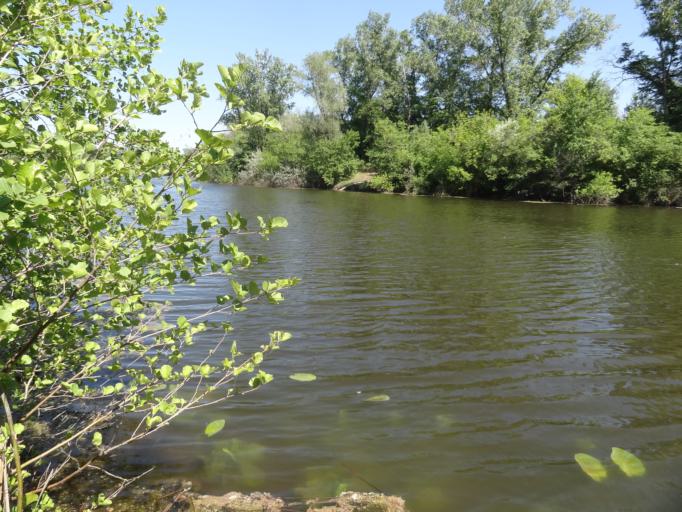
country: RU
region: Saratov
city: Engel's
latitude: 51.4665
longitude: 46.0810
